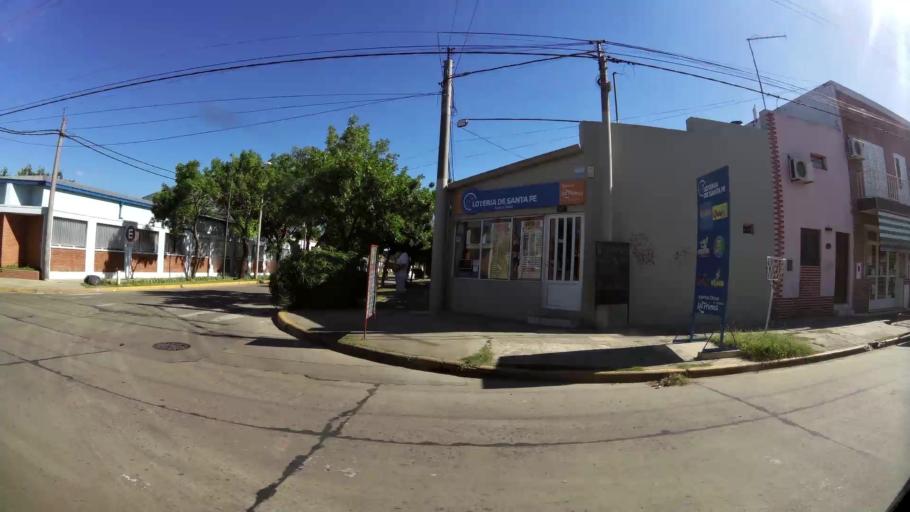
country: AR
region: Santa Fe
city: Rafaela
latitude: -31.2428
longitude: -61.4929
